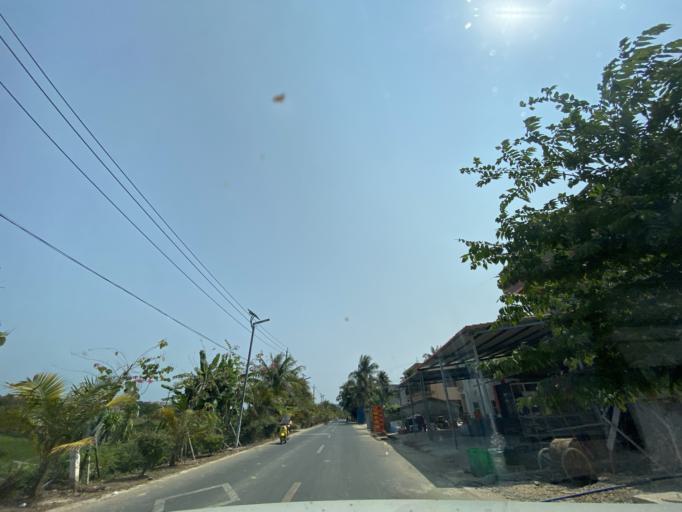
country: CN
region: Hainan
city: Yingzhou
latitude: 18.4147
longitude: 109.8147
